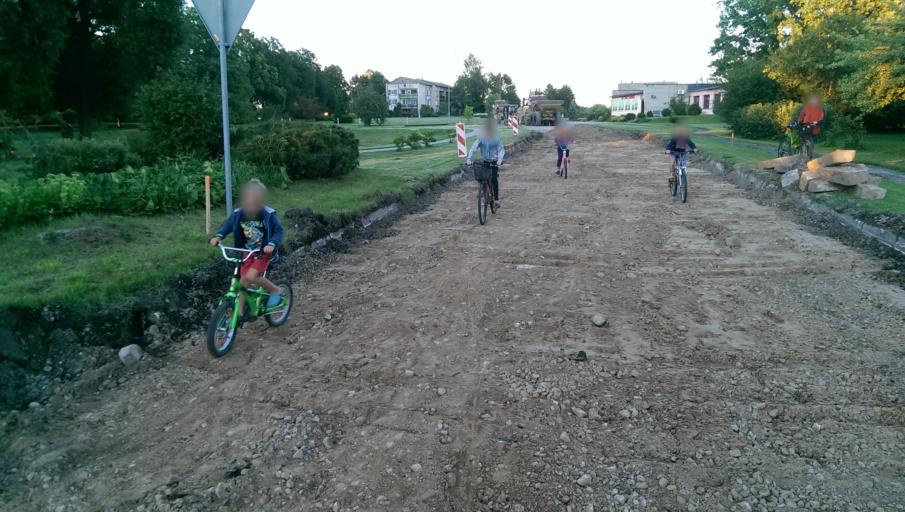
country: LV
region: Aizpute
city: Aizpute
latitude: 56.8356
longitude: 21.7700
